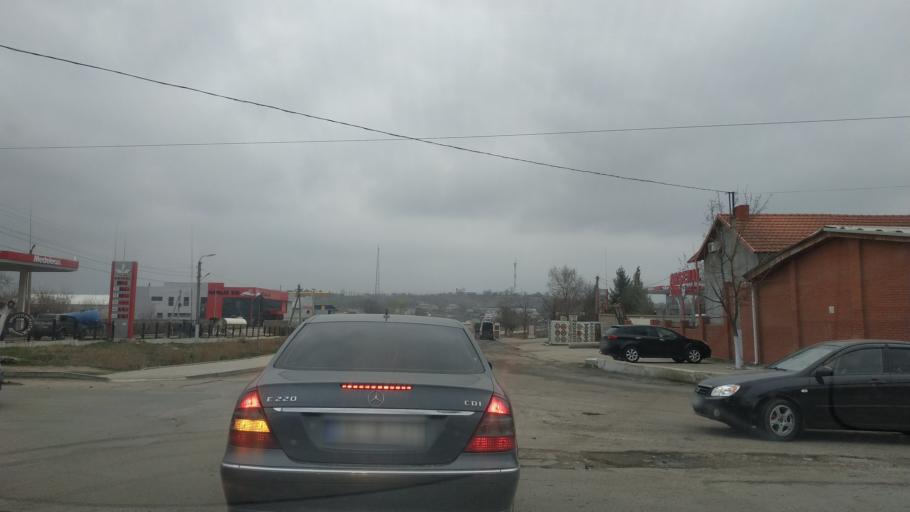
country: MD
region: Gagauzia
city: Comrat
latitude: 46.2947
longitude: 28.6592
